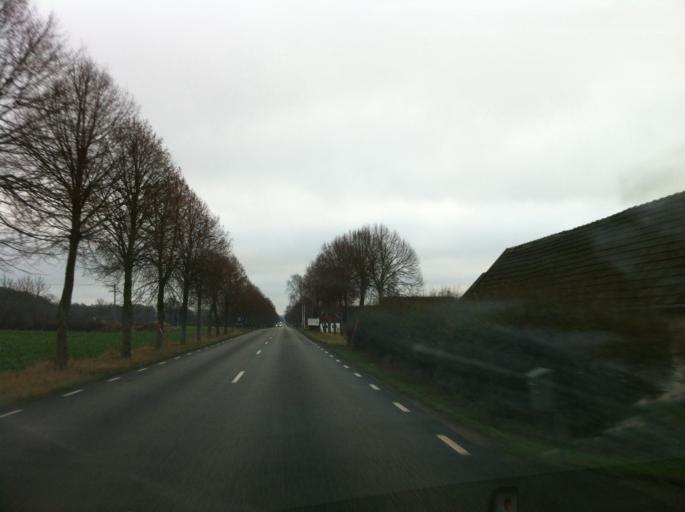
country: SE
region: Skane
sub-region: Hoors Kommun
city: Loberod
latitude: 55.7050
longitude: 13.5641
